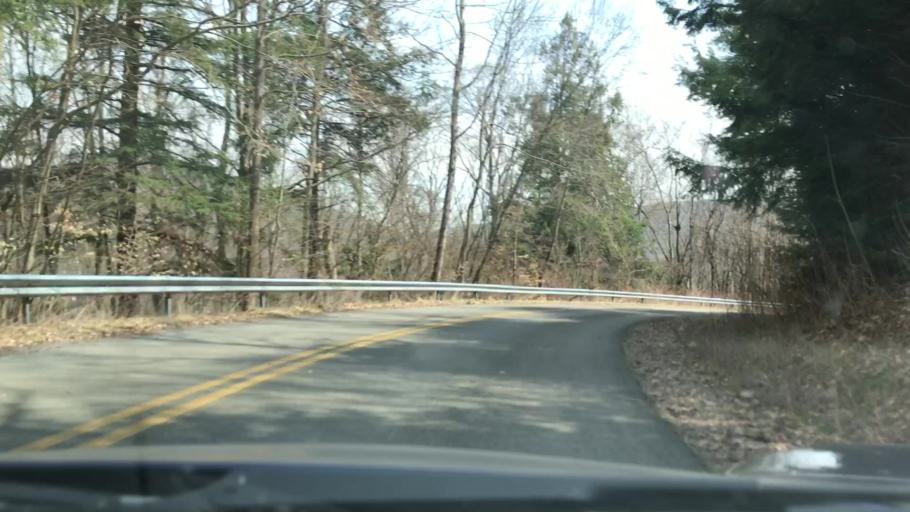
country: US
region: Pennsylvania
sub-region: Warren County
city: Sheffield
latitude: 41.8156
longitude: -78.9441
